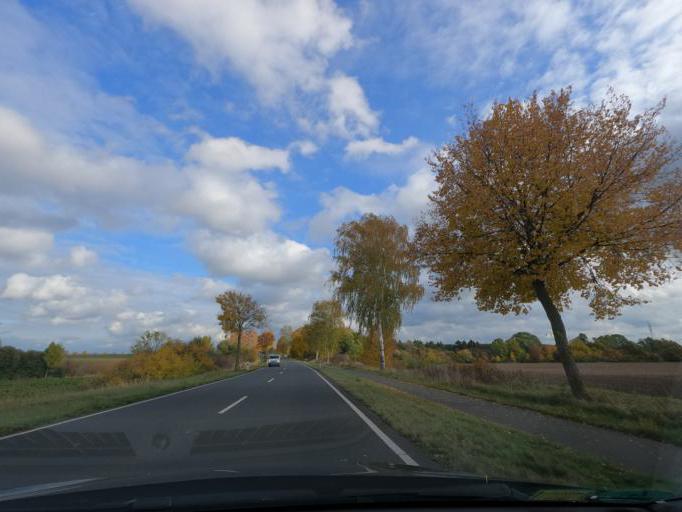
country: DE
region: Lower Saxony
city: Cramme
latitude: 52.1480
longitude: 10.4771
